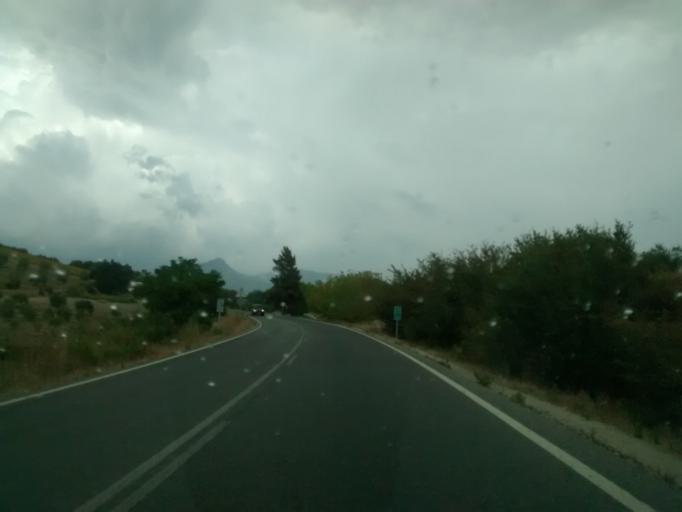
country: ES
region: Andalusia
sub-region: Provincia de Cadiz
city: Prado del Rey
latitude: 36.7901
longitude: -5.5376
